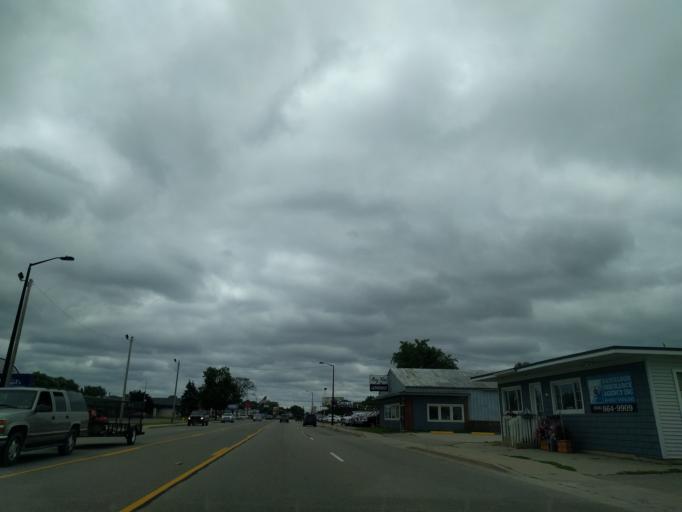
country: US
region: Michigan
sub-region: Menominee County
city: Menominee
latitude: 45.1239
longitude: -87.6132
